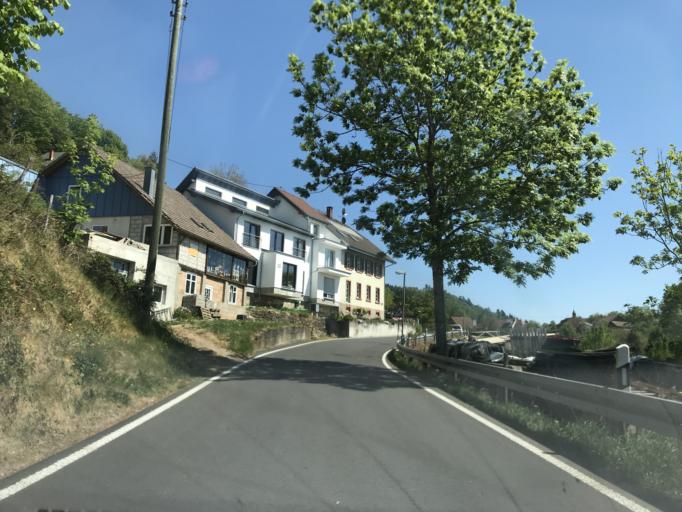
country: DE
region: Baden-Wuerttemberg
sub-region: Freiburg Region
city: Hausen
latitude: 47.6823
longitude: 7.8630
